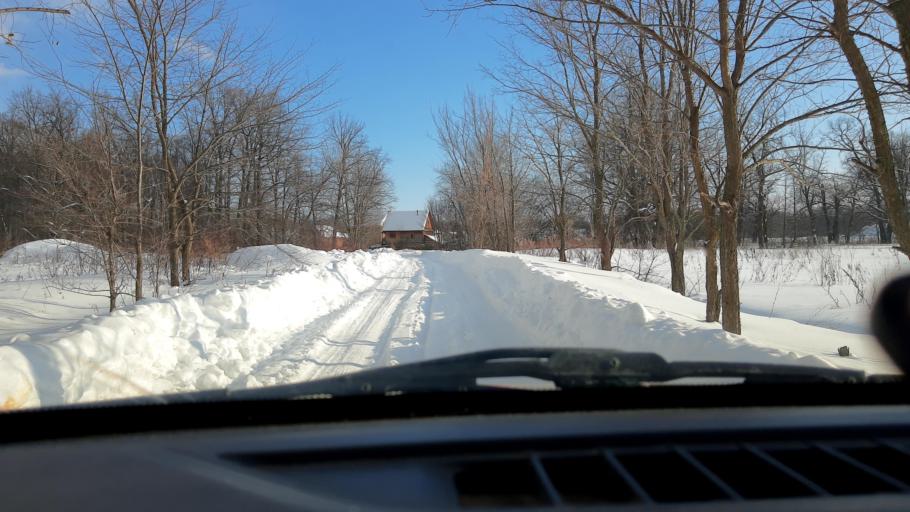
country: RU
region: Bashkortostan
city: Ufa
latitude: 54.6326
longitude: 56.0065
